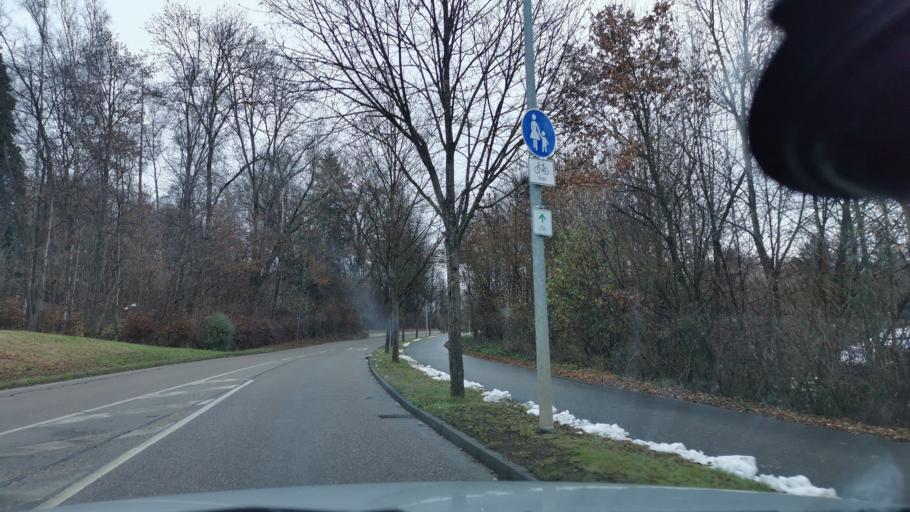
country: DE
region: Baden-Wuerttemberg
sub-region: Regierungsbezirk Stuttgart
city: Goeppingen
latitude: 48.7051
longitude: 9.6776
